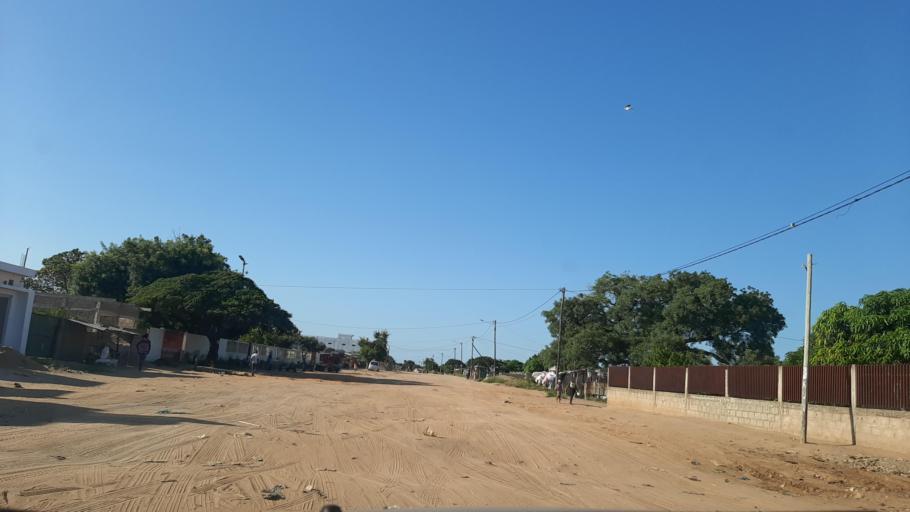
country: MZ
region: Maputo City
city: Maputo
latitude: -25.8084
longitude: 32.5462
